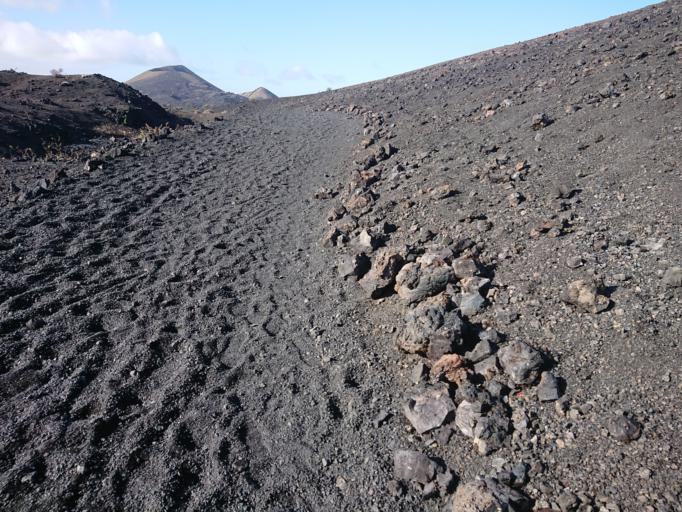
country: ES
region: Canary Islands
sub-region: Provincia de Las Palmas
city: Tias
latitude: 28.9896
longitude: -13.6932
